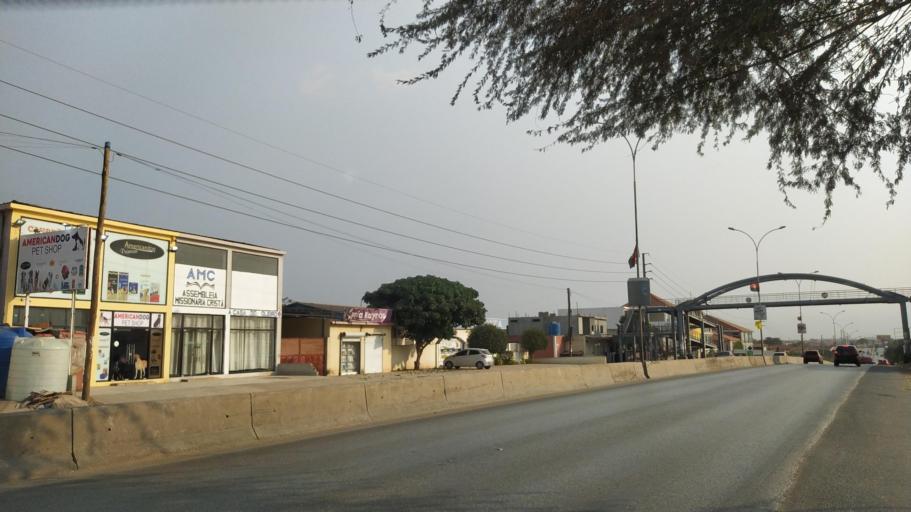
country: AO
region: Luanda
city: Luanda
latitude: -8.9174
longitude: 13.2284
